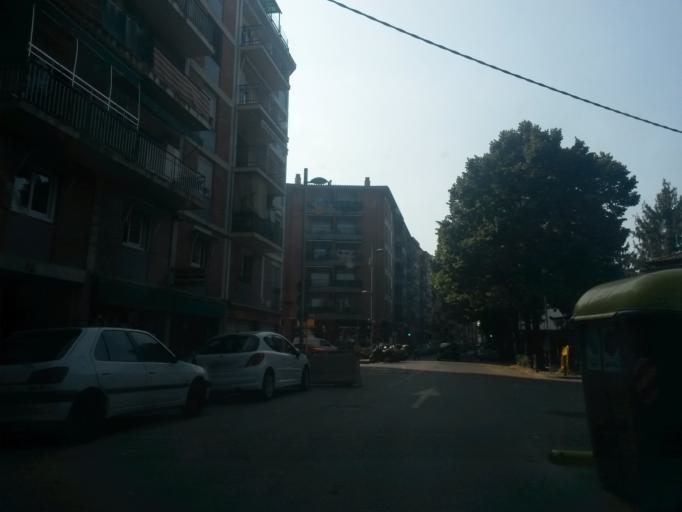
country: ES
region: Catalonia
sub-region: Provincia de Girona
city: Girona
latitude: 41.9753
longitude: 2.8134
